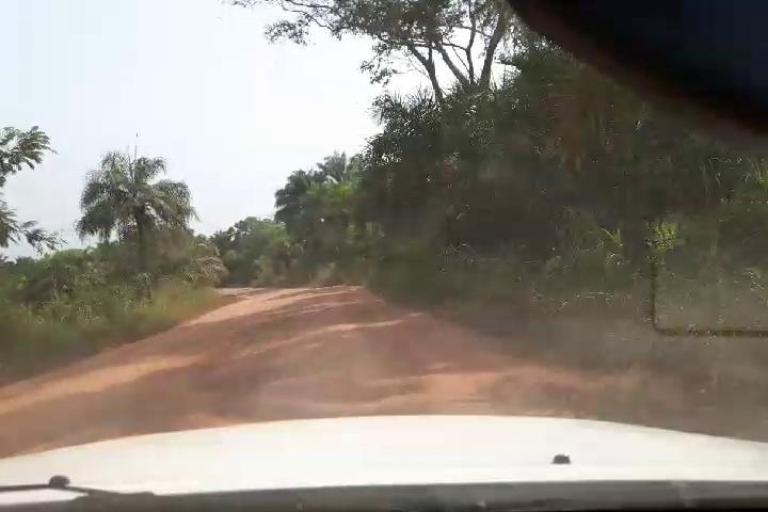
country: SL
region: Northern Province
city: Masingbi
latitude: 8.7763
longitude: -11.8752
